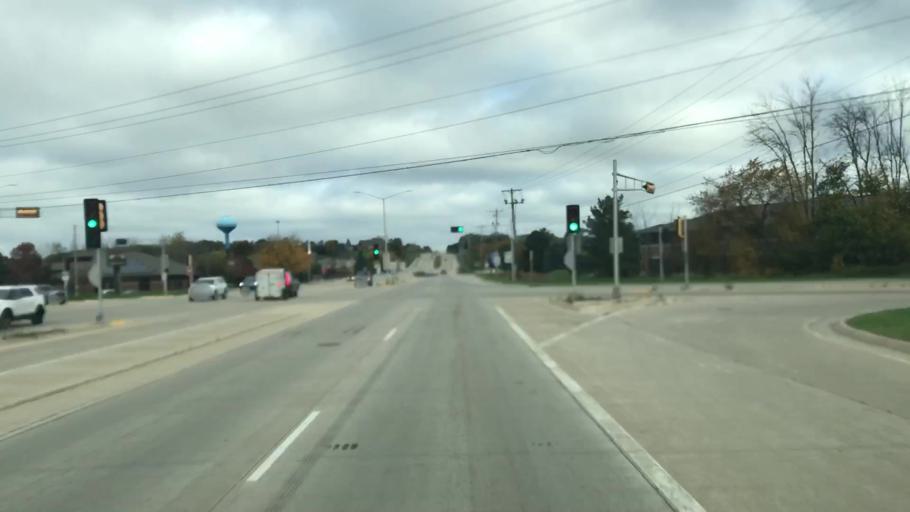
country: US
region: Wisconsin
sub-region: Waukesha County
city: Pewaukee
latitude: 43.0680
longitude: -88.2249
